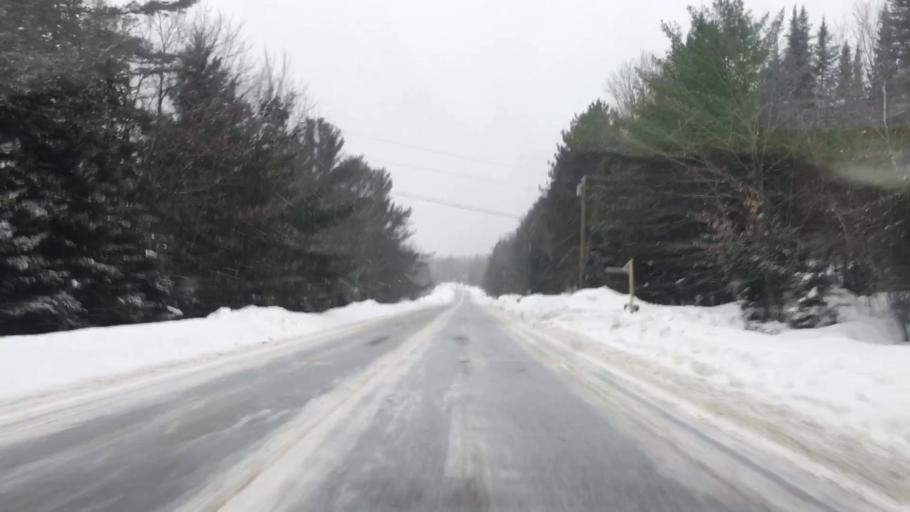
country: US
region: Maine
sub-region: Penobscot County
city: Medway
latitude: 45.5392
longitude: -68.3675
